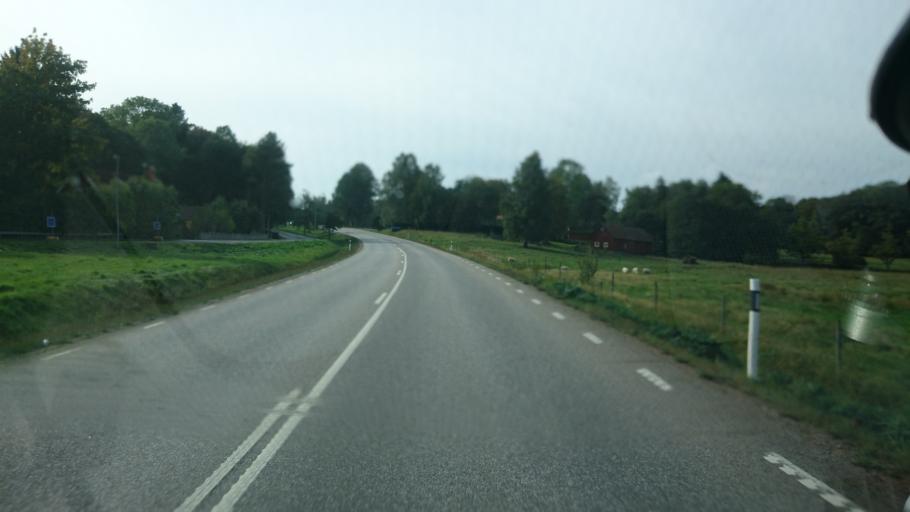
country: SE
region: Vaestra Goetaland
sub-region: Alingsas Kommun
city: Sollebrunn
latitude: 58.0842
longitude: 12.4900
